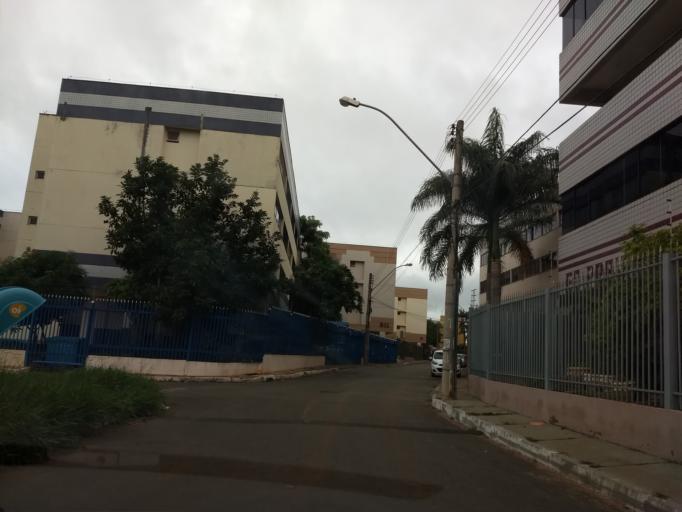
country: BR
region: Federal District
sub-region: Brasilia
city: Brasilia
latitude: -15.8072
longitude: -47.9906
